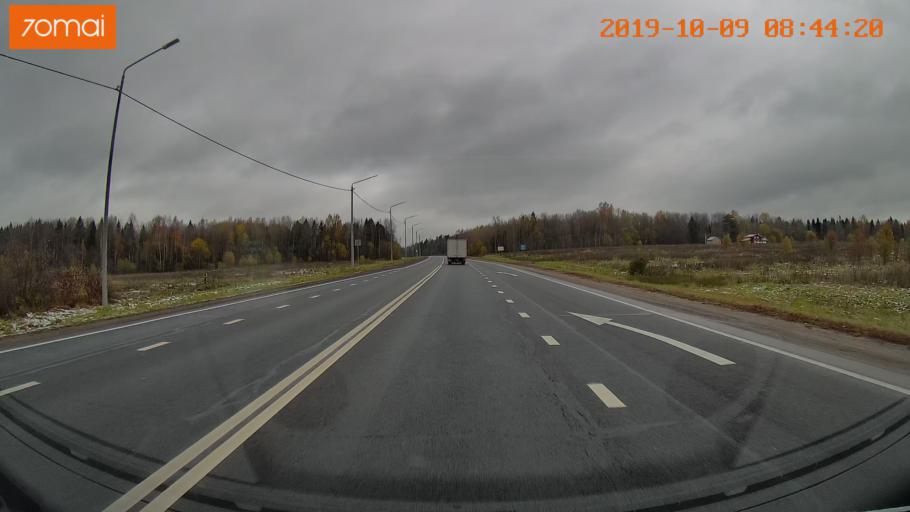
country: RU
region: Vologda
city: Gryazovets
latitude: 59.0353
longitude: 40.1086
